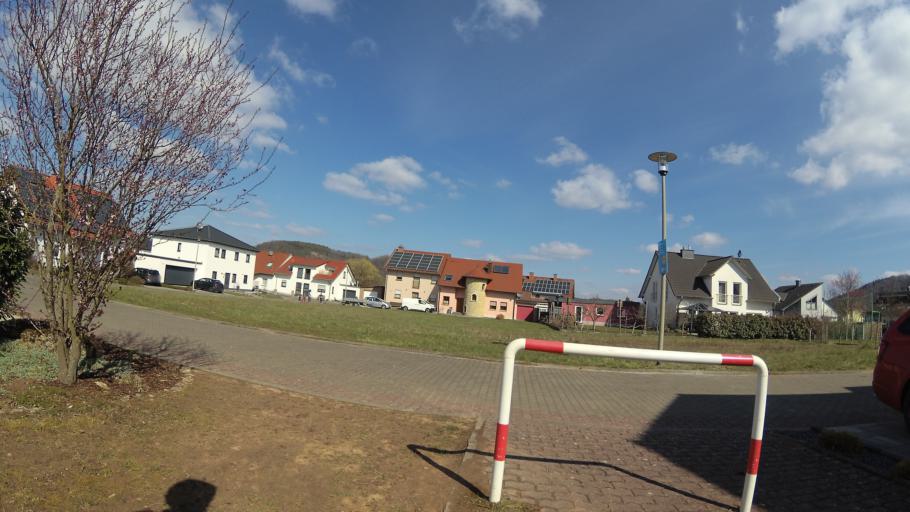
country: DE
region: Saarland
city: Rehlingen-Siersburg
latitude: 49.3588
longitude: 6.6603
